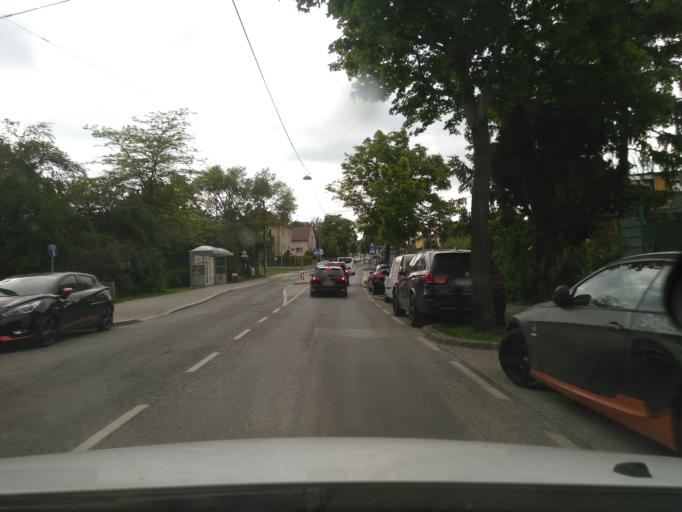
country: AT
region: Lower Austria
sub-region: Politischer Bezirk Modling
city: Perchtoldsdorf
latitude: 48.1536
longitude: 16.2918
